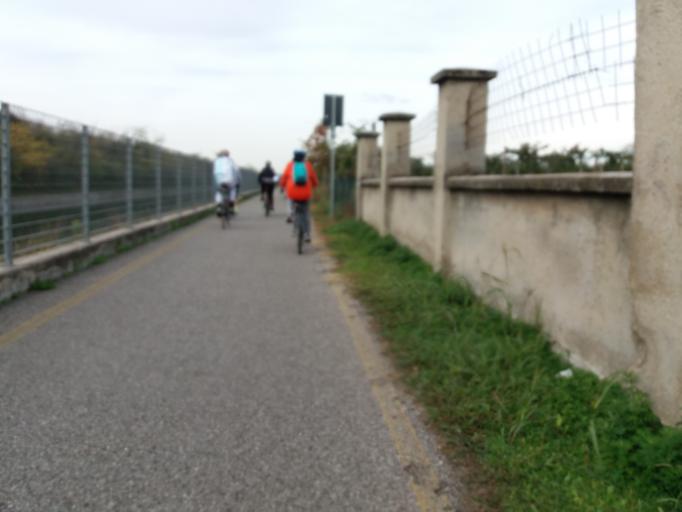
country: IT
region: Veneto
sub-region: Provincia di Verona
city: Settimo
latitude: 45.4641
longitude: 10.9236
